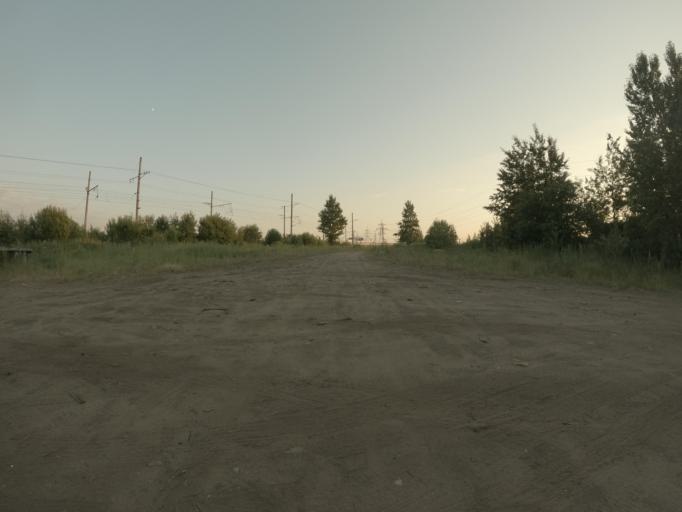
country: RU
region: St.-Petersburg
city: Admiralteisky
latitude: 59.8828
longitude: 30.2916
